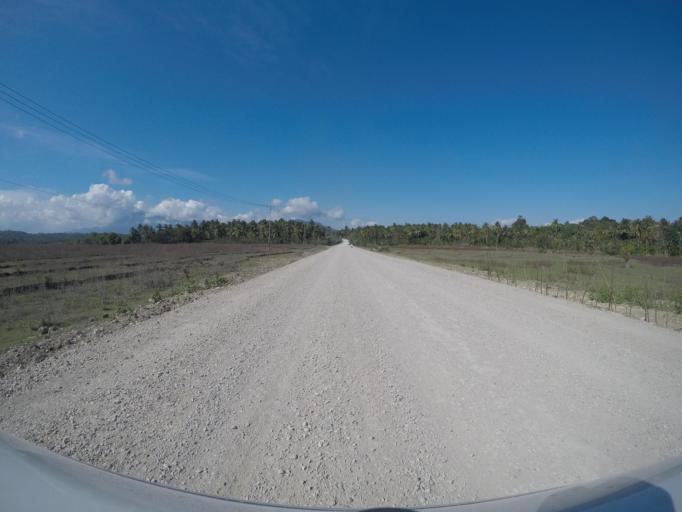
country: TL
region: Viqueque
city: Viqueque
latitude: -8.8300
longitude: 126.5239
